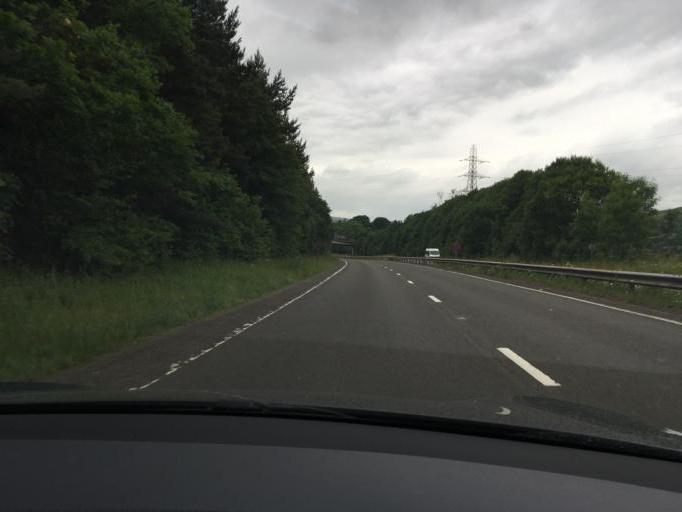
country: GB
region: England
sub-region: Derbyshire
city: Chinley
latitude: 53.3337
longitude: -1.9367
